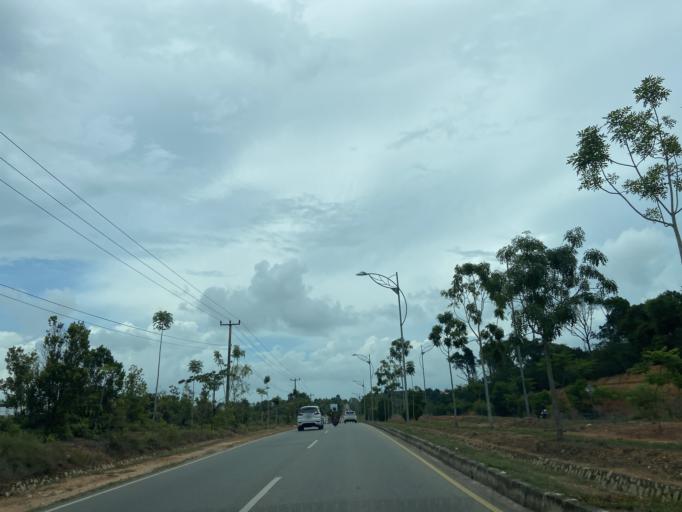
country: SG
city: Singapore
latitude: 1.1387
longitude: 104.1190
